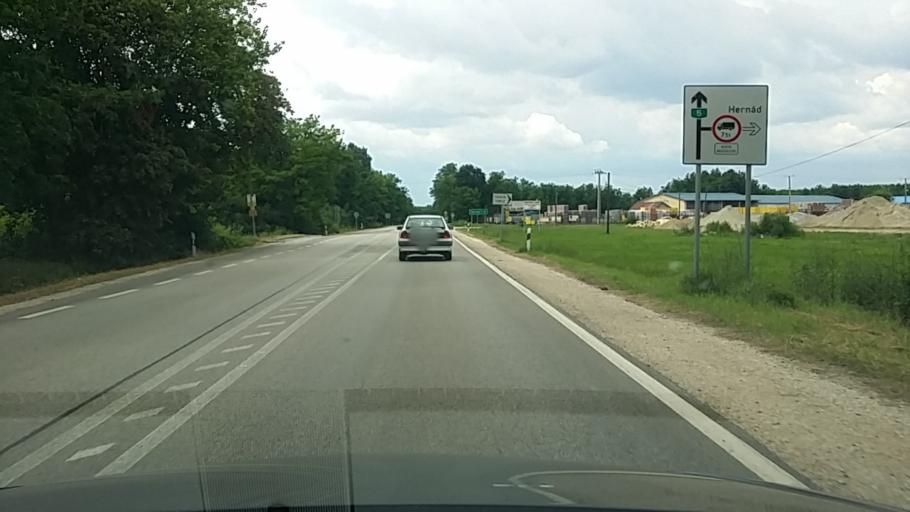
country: HU
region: Pest
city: Hernad
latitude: 47.1505
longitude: 19.3905
